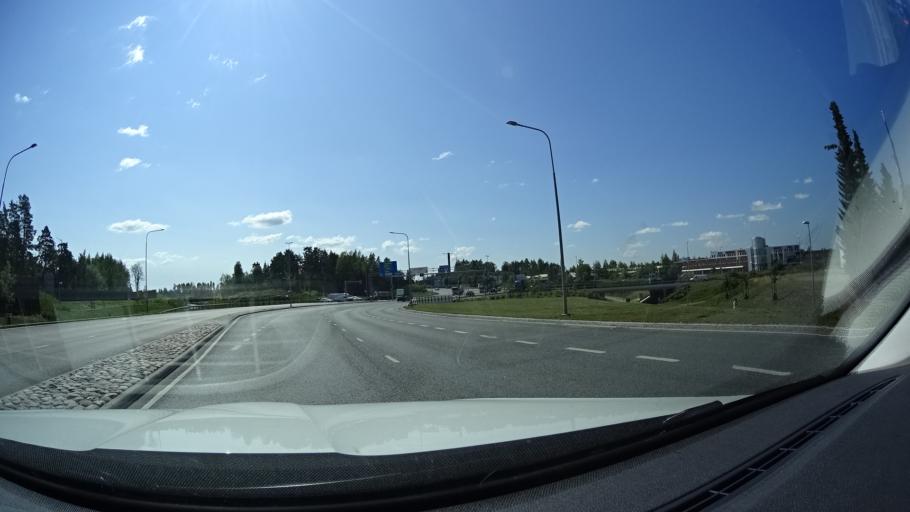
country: FI
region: Uusimaa
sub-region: Helsinki
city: Kerava
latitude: 60.3937
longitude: 25.1124
